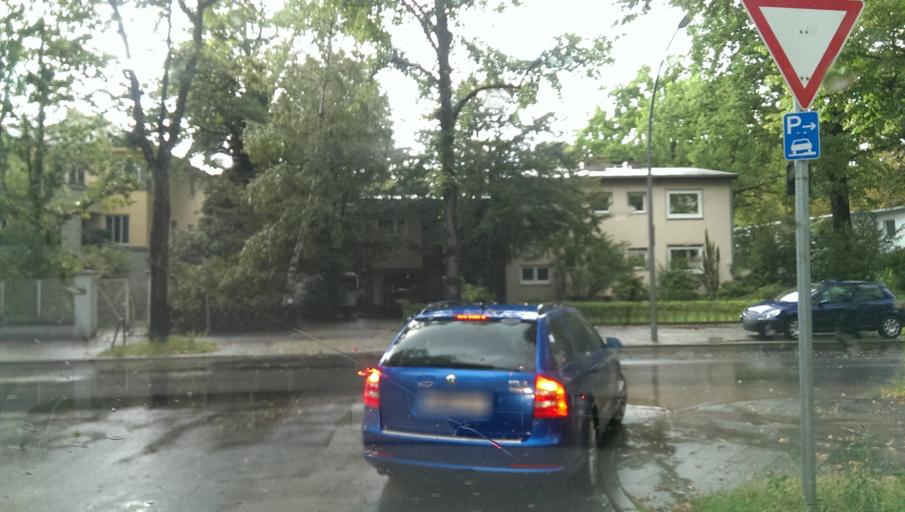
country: DE
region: Berlin
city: Lichterfelde
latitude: 52.4341
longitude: 13.3202
